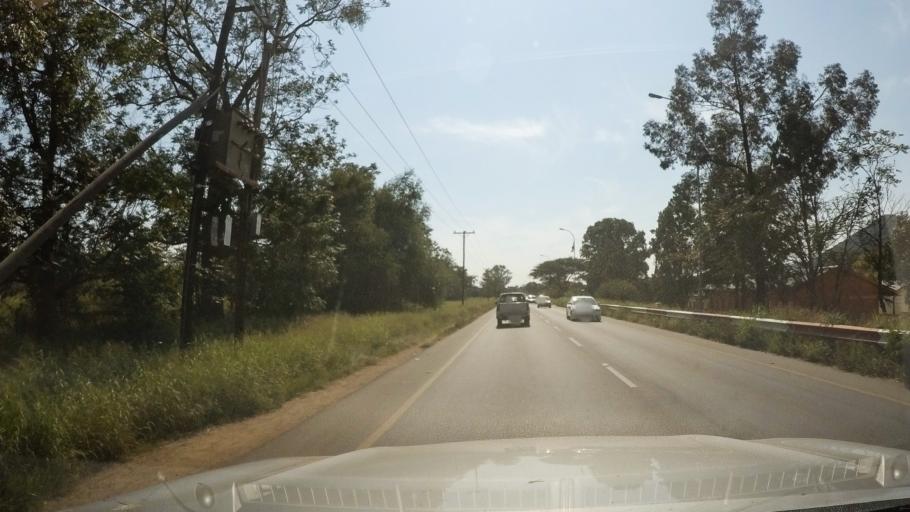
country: BW
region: South East
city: Lobatse
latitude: -25.2195
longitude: 25.6801
